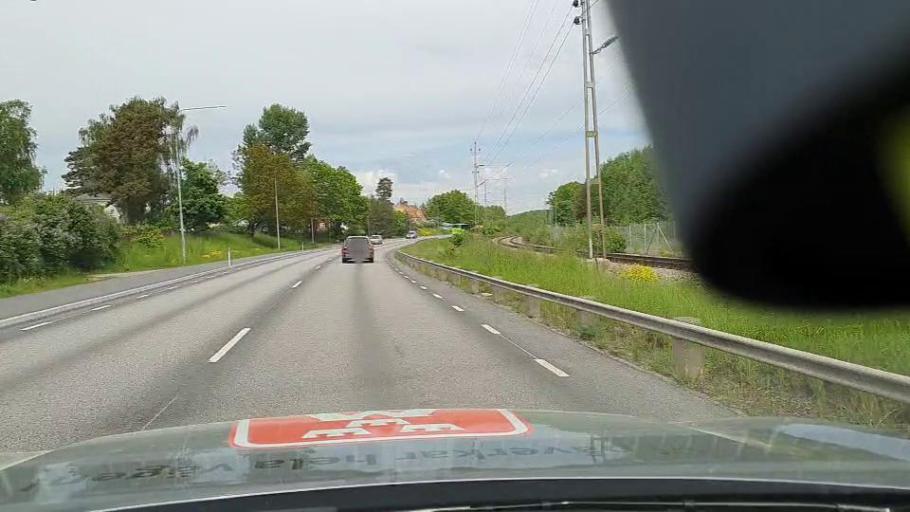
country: SE
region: Soedermanland
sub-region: Flens Kommun
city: Flen
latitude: 59.0696
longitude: 16.5913
